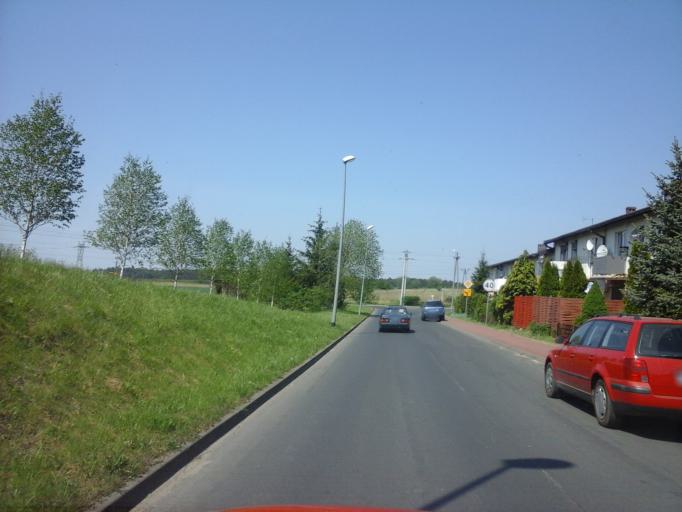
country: PL
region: West Pomeranian Voivodeship
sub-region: Powiat choszczenski
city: Choszczno
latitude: 53.1638
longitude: 15.3967
